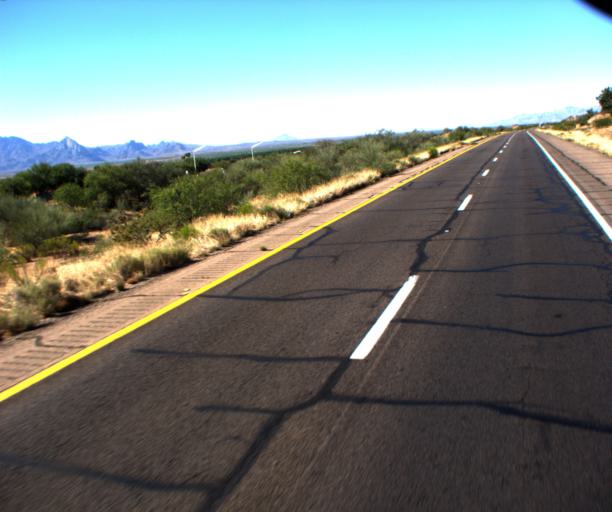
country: US
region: Arizona
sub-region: Pima County
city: Green Valley
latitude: 31.8341
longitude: -111.0005
